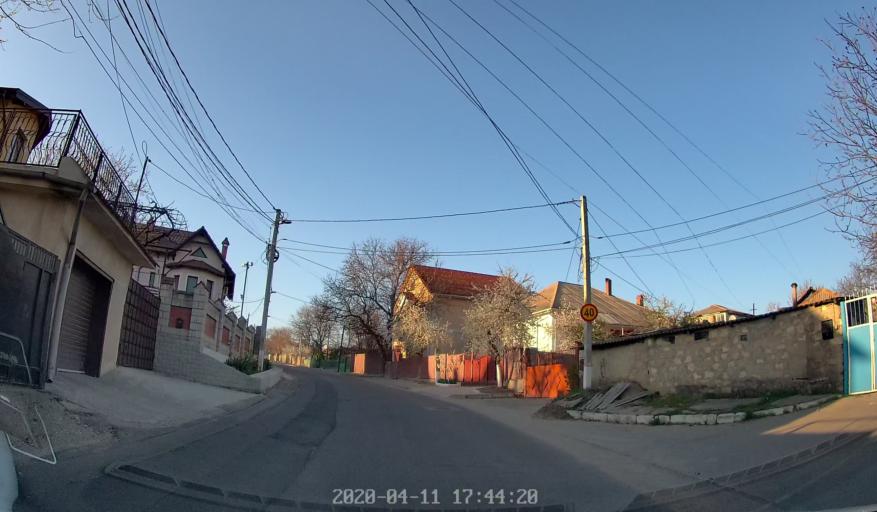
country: MD
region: Chisinau
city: Chisinau
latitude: 46.9774
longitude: 28.8240
